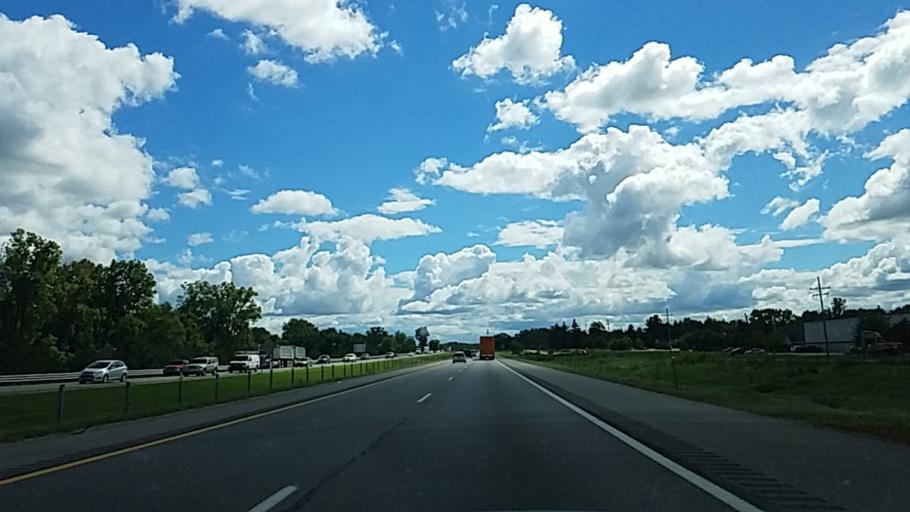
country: US
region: Michigan
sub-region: Livingston County
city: Brighton
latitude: 42.4926
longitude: -83.7577
